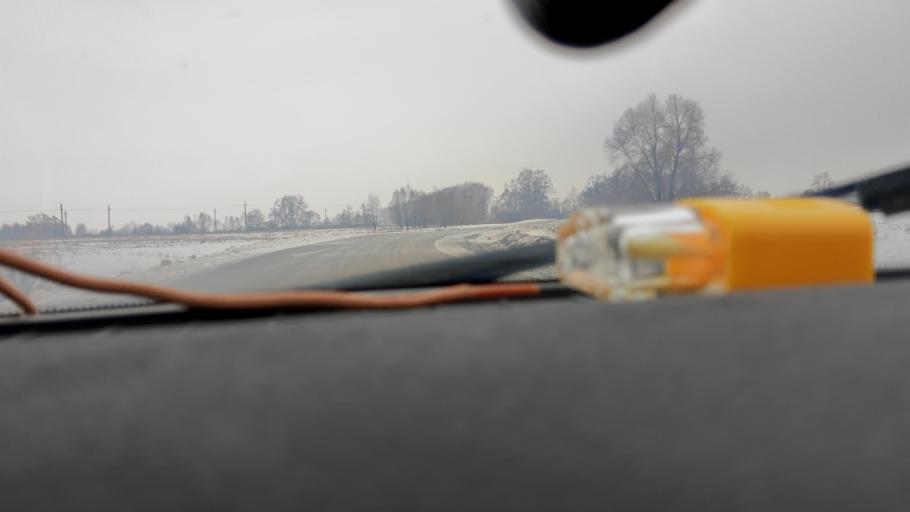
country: RU
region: Bashkortostan
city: Ulukulevo
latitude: 54.5079
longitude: 56.4097
